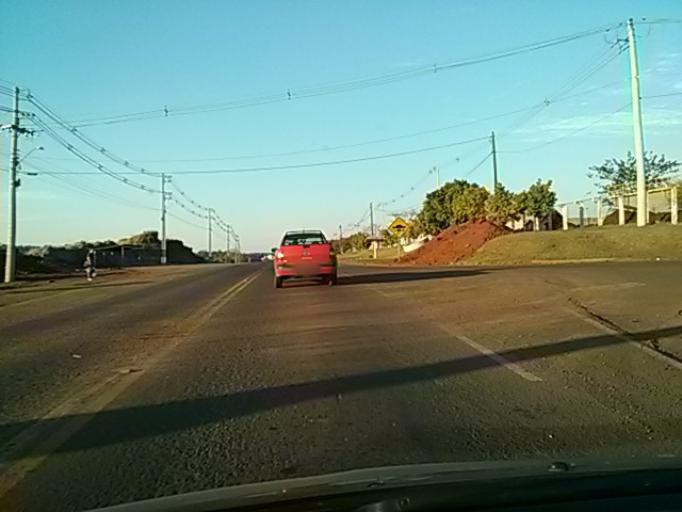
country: BR
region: Santa Catarina
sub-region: Chapeco
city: Chapeco
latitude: -27.0986
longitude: -52.6946
